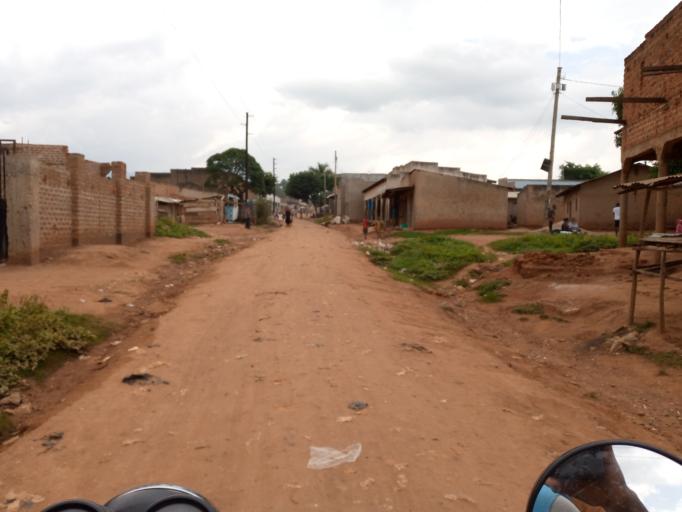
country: UG
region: Eastern Region
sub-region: Mbale District
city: Mbale
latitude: 1.0863
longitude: 34.1657
